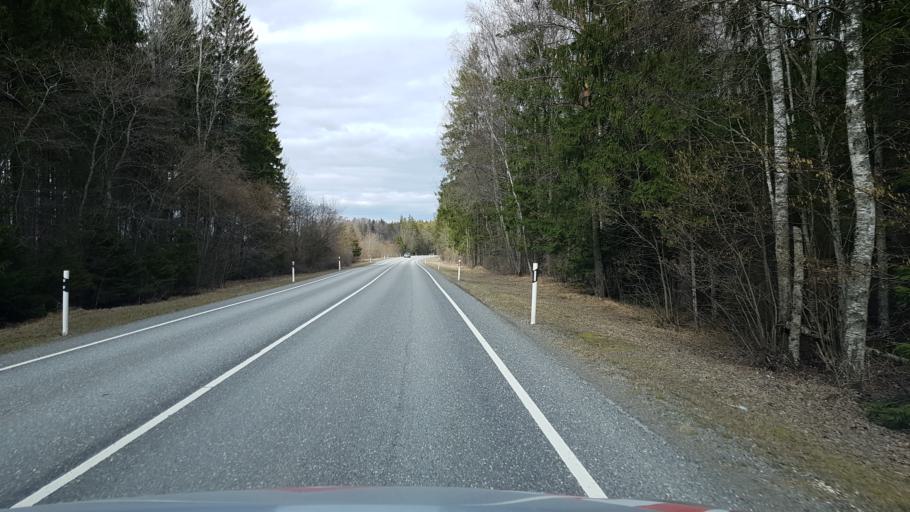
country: EE
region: Laeaene-Virumaa
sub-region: Vaeike-Maarja vald
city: Vaike-Maarja
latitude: 59.0669
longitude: 26.2387
